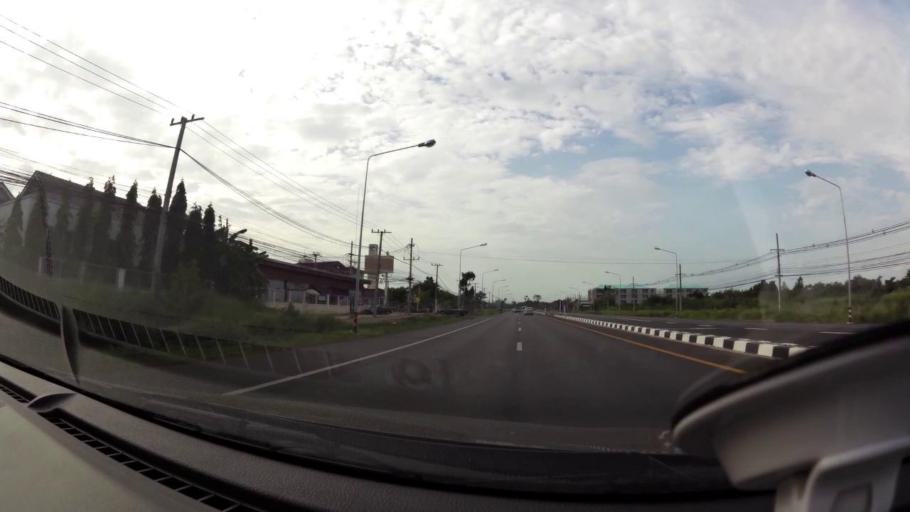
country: TH
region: Prachuap Khiri Khan
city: Hua Hin
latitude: 12.4758
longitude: 99.9714
